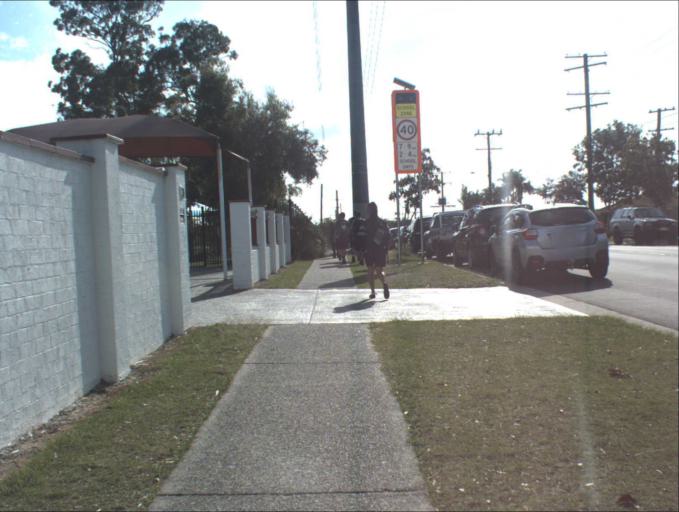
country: AU
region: Queensland
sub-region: Logan
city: Woodridge
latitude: -27.6678
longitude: 153.0556
